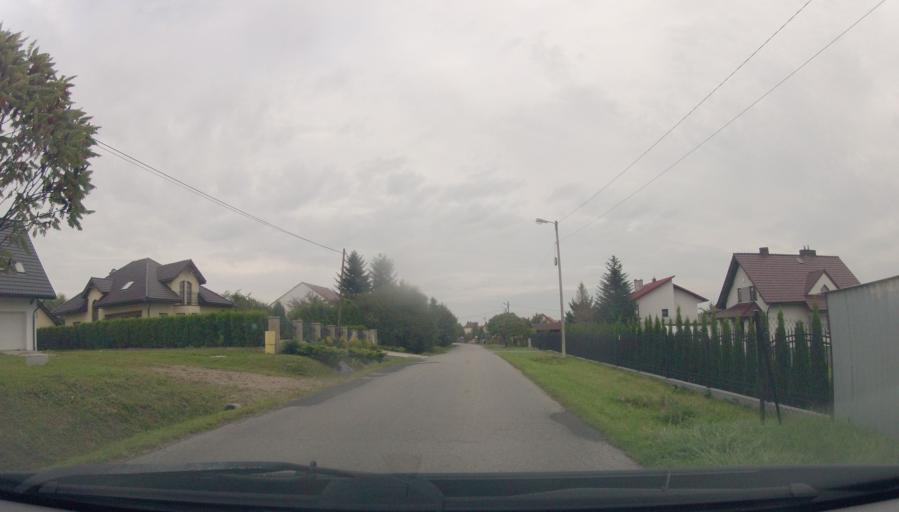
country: PL
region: Lesser Poland Voivodeship
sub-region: Powiat wielicki
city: Pawlikowice
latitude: 49.9513
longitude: 20.0196
